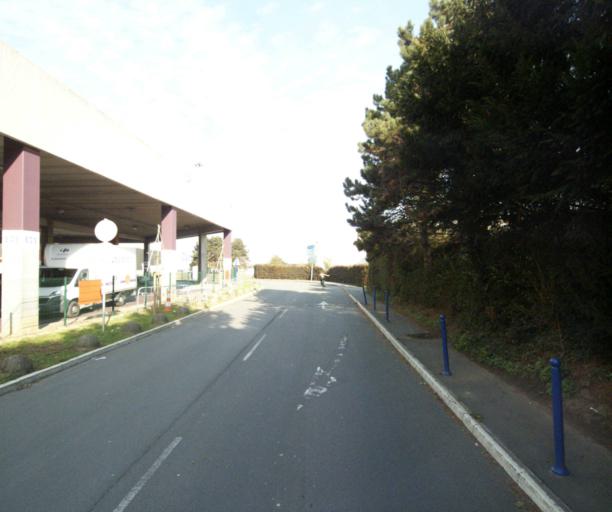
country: FR
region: Nord-Pas-de-Calais
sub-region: Departement du Nord
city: Lomme
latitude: 50.6510
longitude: 2.9806
